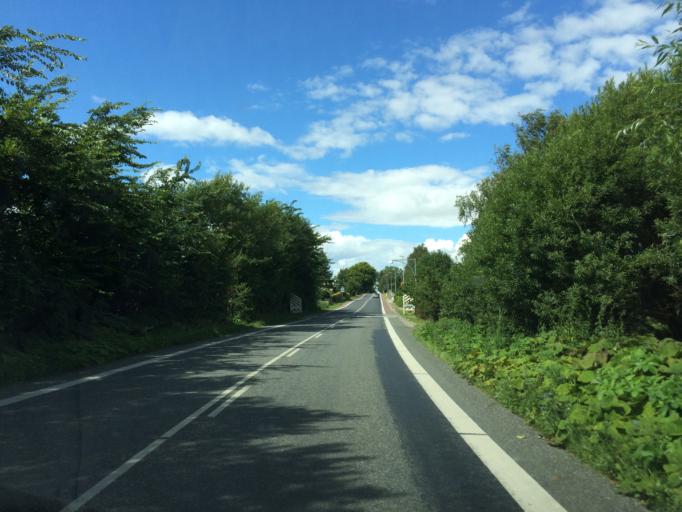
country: DK
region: South Denmark
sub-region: Assens Kommune
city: Harby
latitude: 55.1399
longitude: 10.1642
